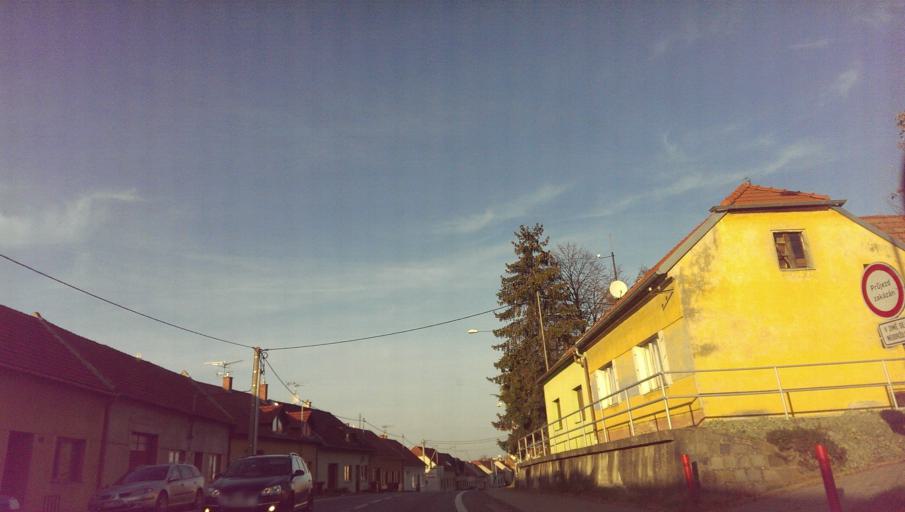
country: CZ
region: Zlin
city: Kunovice
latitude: 49.0373
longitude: 17.4618
